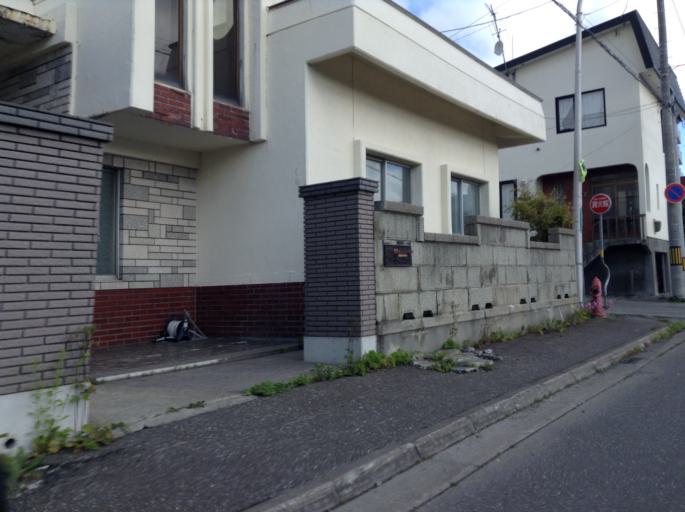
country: JP
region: Hokkaido
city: Wakkanai
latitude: 45.4086
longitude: 141.6745
